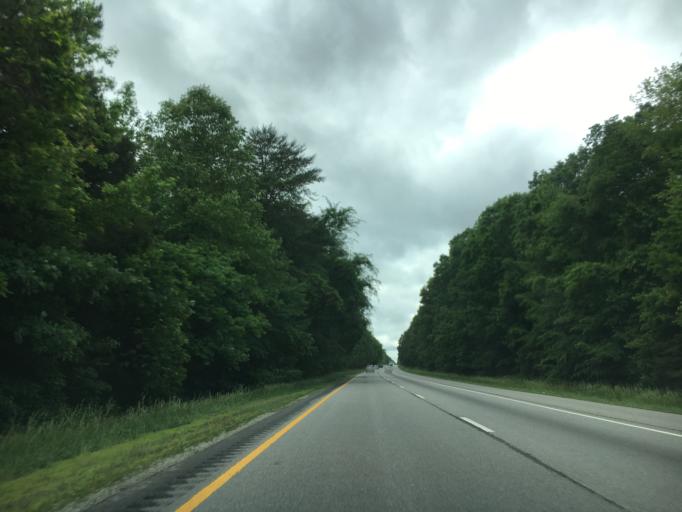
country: US
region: Virginia
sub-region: Mecklenburg County
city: South Hill
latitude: 36.7753
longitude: -78.0313
